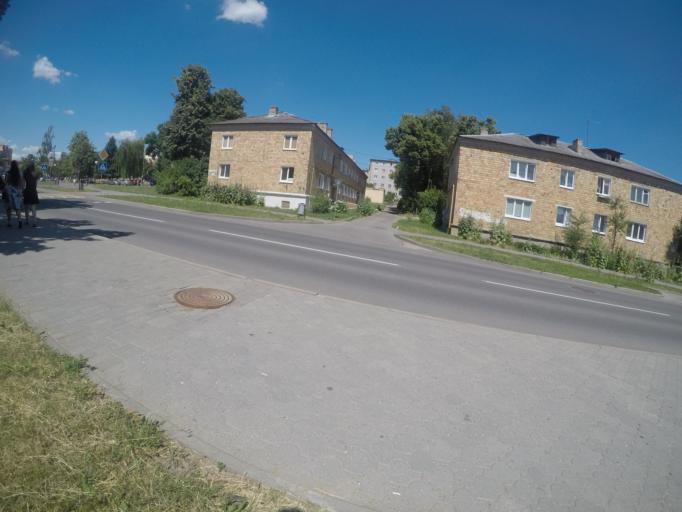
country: BY
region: Grodnenskaya
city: Hrodna
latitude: 53.6929
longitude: 23.8297
